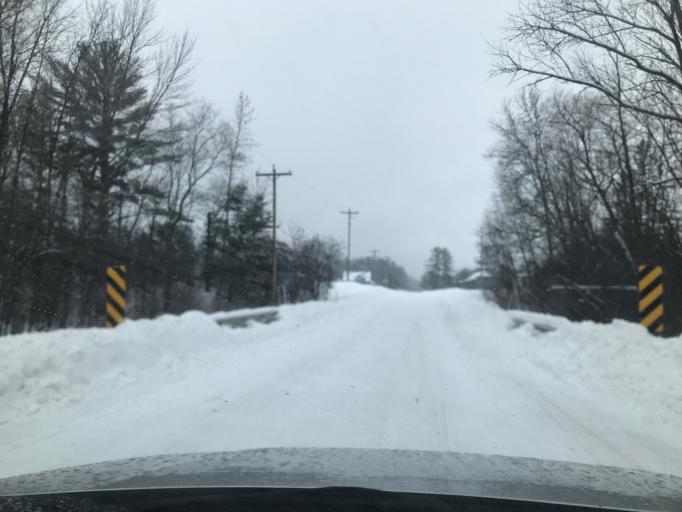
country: US
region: Wisconsin
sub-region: Marinette County
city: Peshtigo
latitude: 45.3802
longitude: -87.9470
